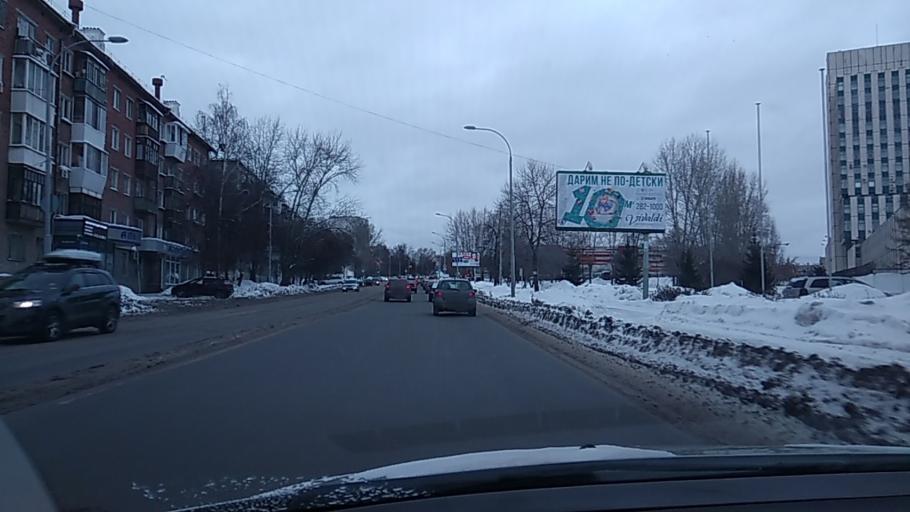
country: RU
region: Sverdlovsk
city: Yekaterinburg
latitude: 56.8195
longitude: 60.6402
